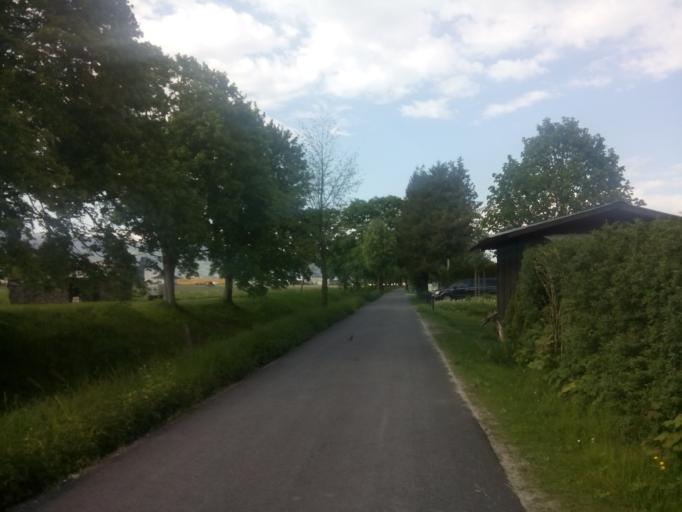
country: AT
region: Vorarlberg
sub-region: Politischer Bezirk Feldkirch
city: Koblach
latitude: 47.3408
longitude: 9.5937
